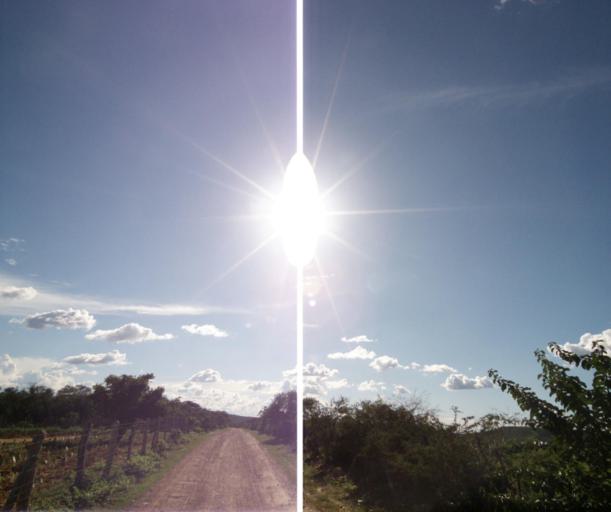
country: BR
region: Bahia
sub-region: Tanhacu
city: Tanhacu
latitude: -14.1866
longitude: -40.9402
